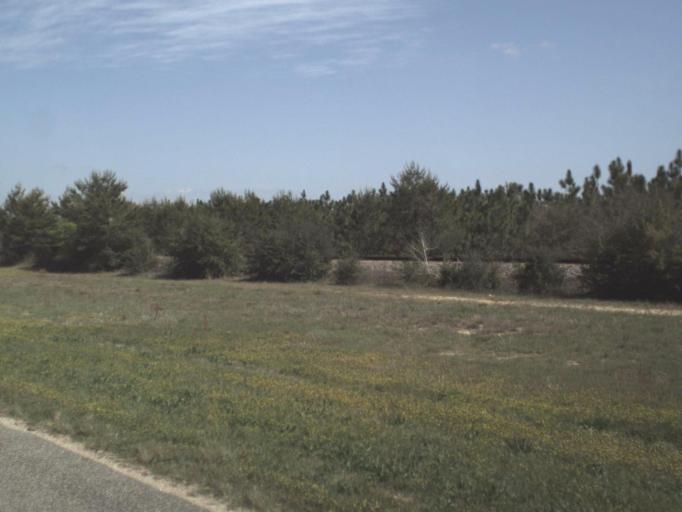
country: US
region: Florida
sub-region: Okaloosa County
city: Crestview
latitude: 30.7515
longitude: -86.4412
